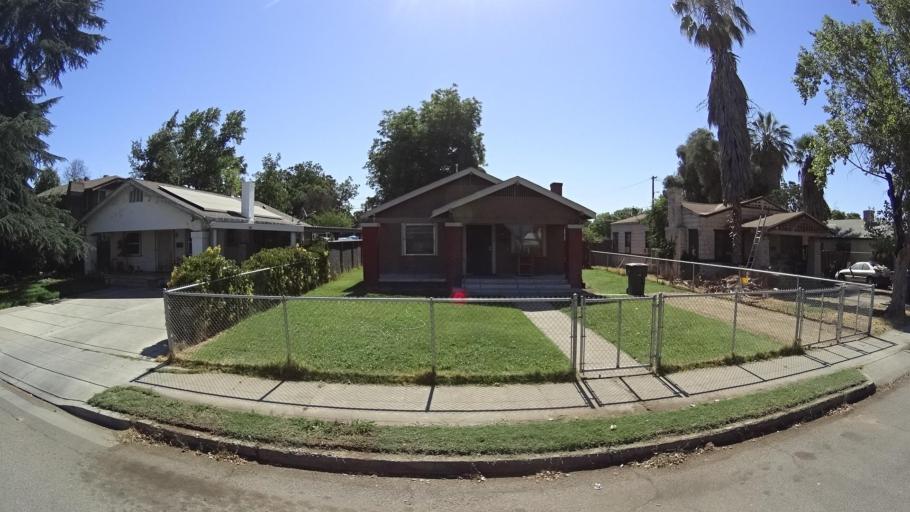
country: US
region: California
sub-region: Fresno County
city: Fresno
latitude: 36.7473
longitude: -119.8070
